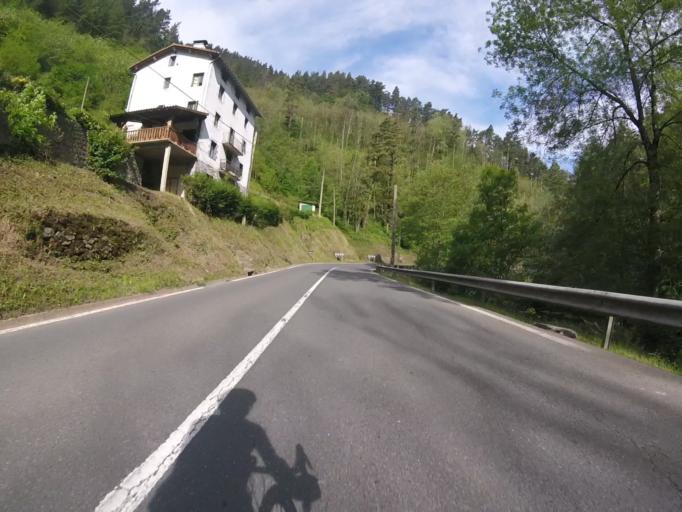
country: ES
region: Basque Country
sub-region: Provincia de Guipuzcoa
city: Anzuola
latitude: 43.1302
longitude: -2.3512
